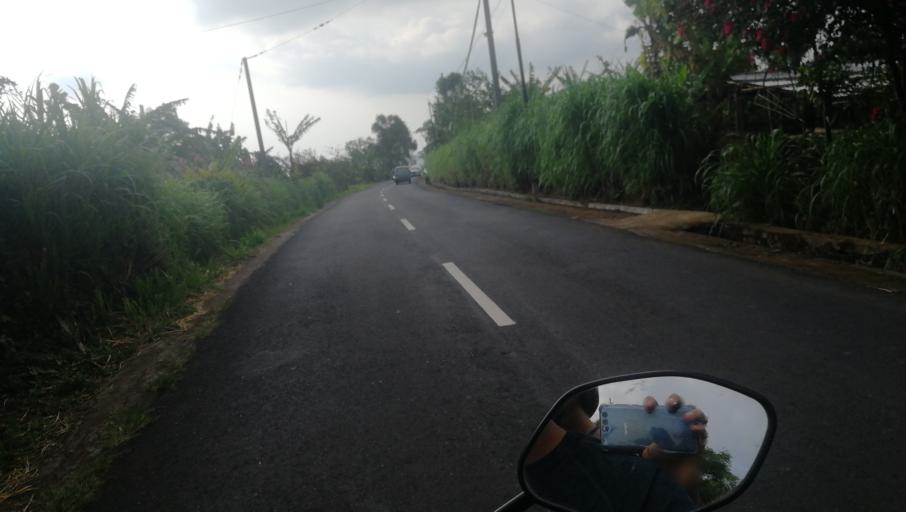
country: ID
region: Bali
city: Munduk
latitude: -8.2594
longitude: 115.0787
